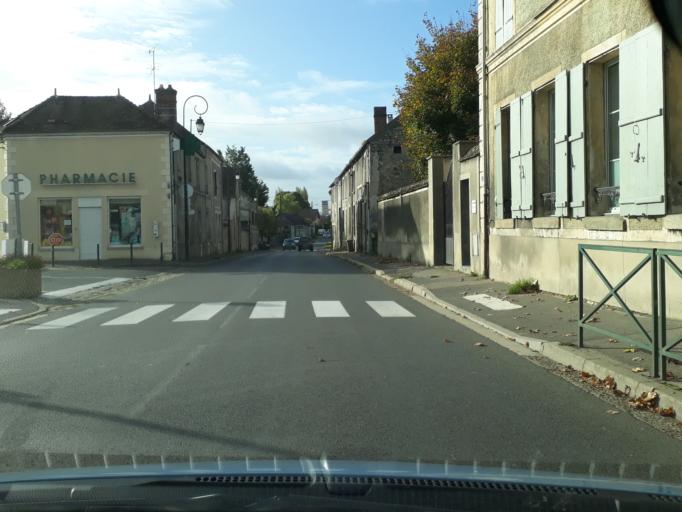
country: FR
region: Ile-de-France
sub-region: Departement de Seine-et-Marne
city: Acheres-la-Foret
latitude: 48.3429
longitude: 2.6014
